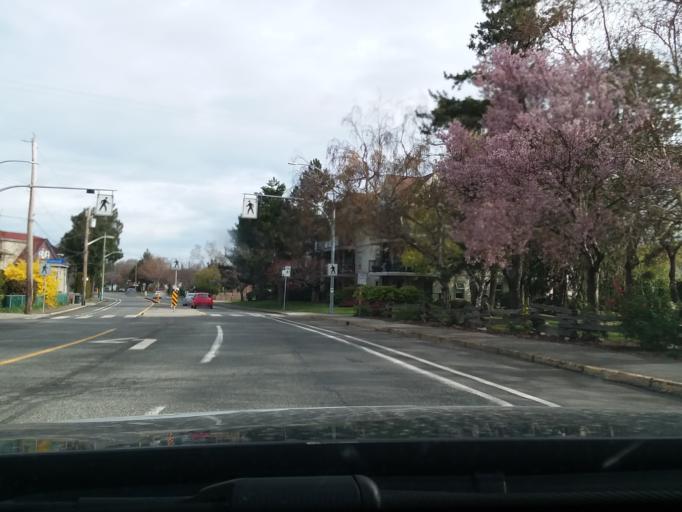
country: CA
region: British Columbia
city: Oak Bay
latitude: 48.4308
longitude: -123.3330
